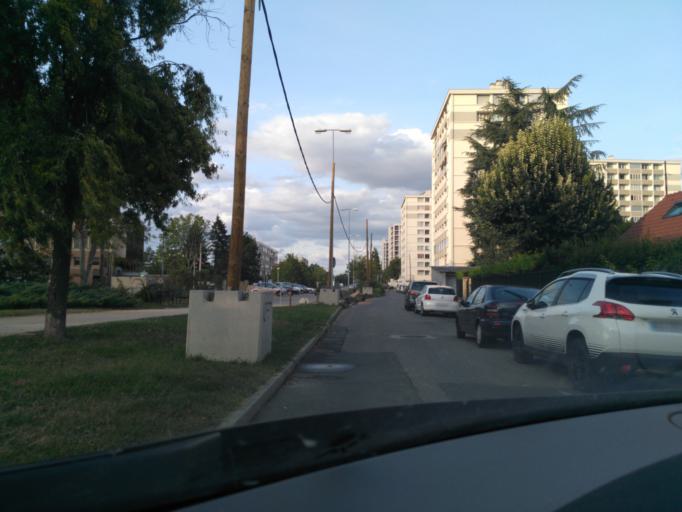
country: FR
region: Rhone-Alpes
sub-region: Departement du Rhone
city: Caluire-et-Cuire
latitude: 45.7929
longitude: 4.8431
